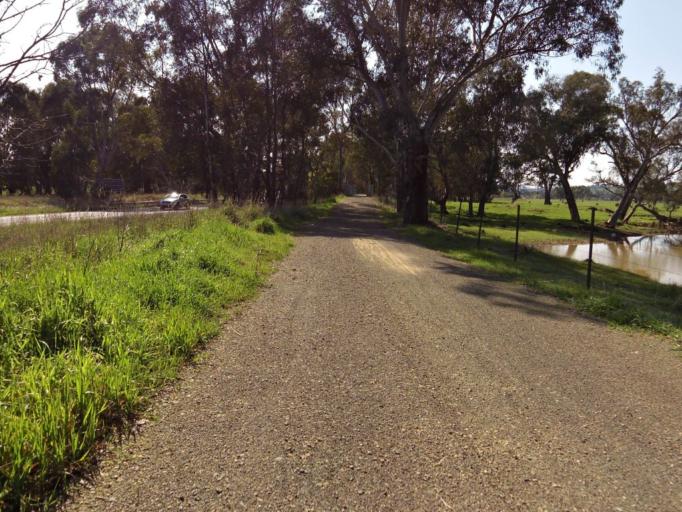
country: AU
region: Victoria
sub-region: Murrindindi
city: Alexandra
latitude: -37.1520
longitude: 145.5793
